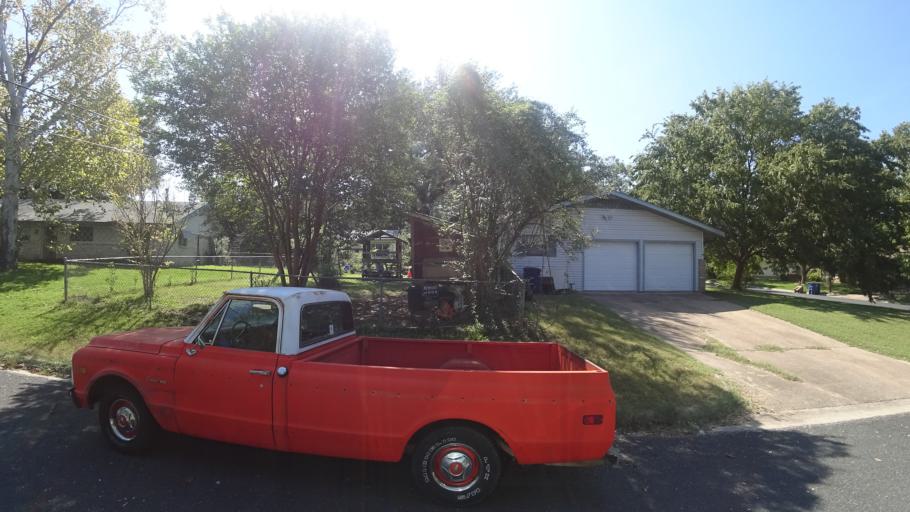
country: US
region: Texas
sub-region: Travis County
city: Austin
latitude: 30.3181
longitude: -97.6833
